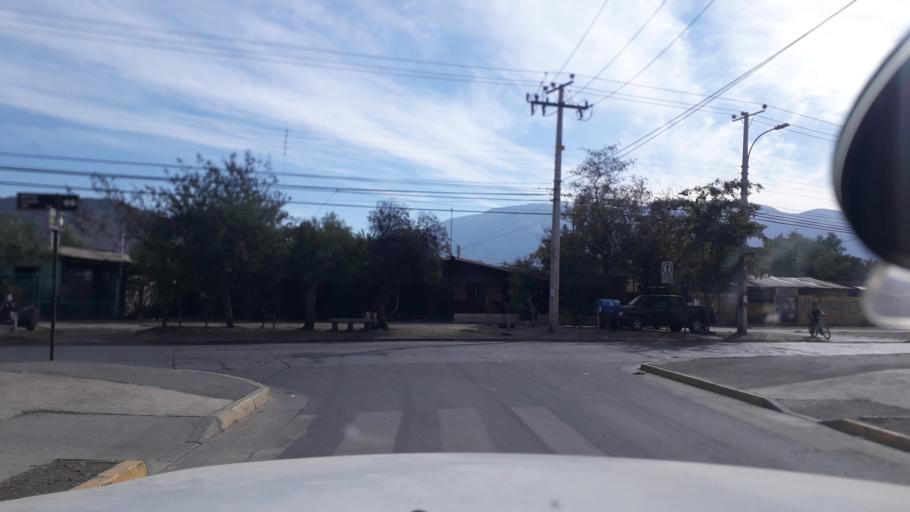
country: CL
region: Valparaiso
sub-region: Provincia de San Felipe
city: San Felipe
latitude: -32.7467
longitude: -70.7338
